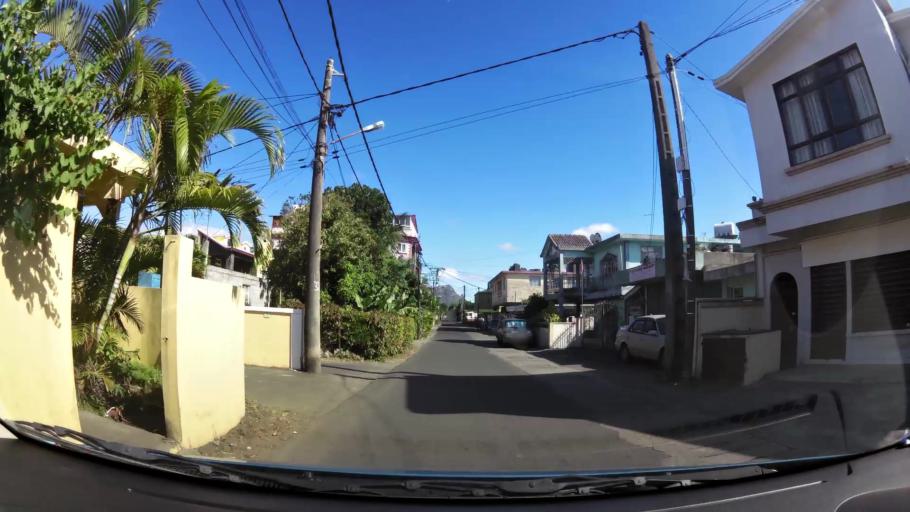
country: MU
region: Plaines Wilhems
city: Quatre Bornes
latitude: -20.2788
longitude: 57.4688
